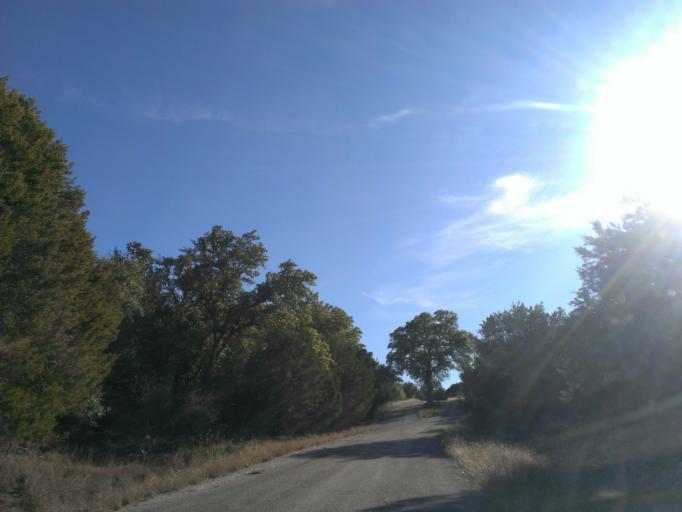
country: US
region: Texas
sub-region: Llano County
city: Horseshoe Bay
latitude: 30.5358
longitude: -98.3361
